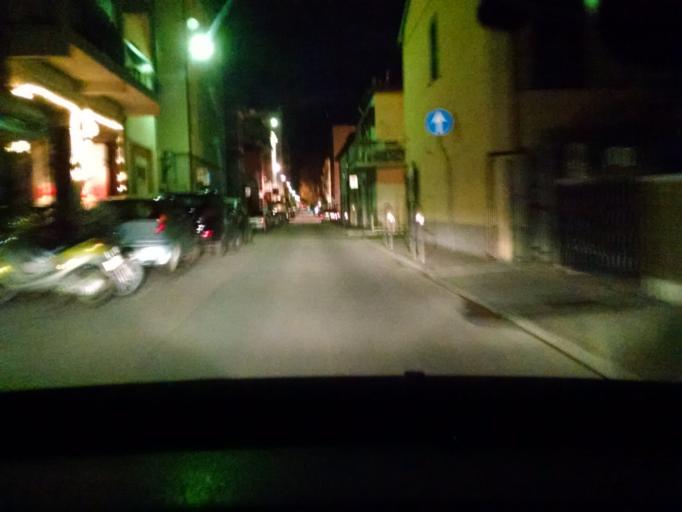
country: IT
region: Tuscany
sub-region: Provincia di Grosseto
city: Follonica
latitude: 42.9221
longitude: 10.7562
